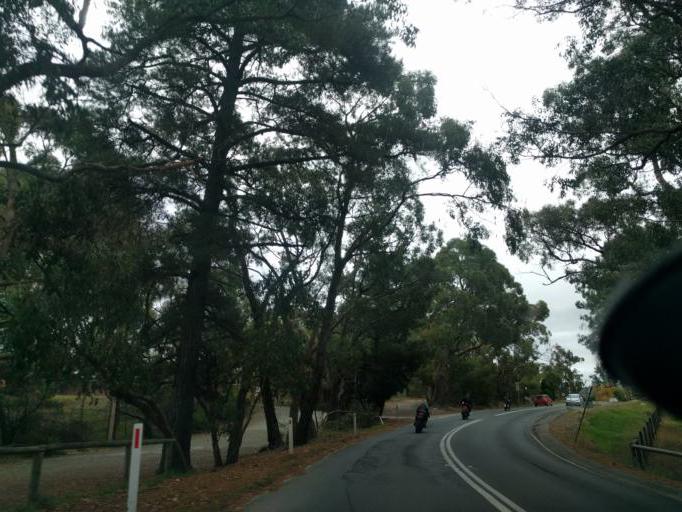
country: AU
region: South Australia
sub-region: Adelaide Hills
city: Stirling
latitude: -35.0195
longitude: 138.7505
